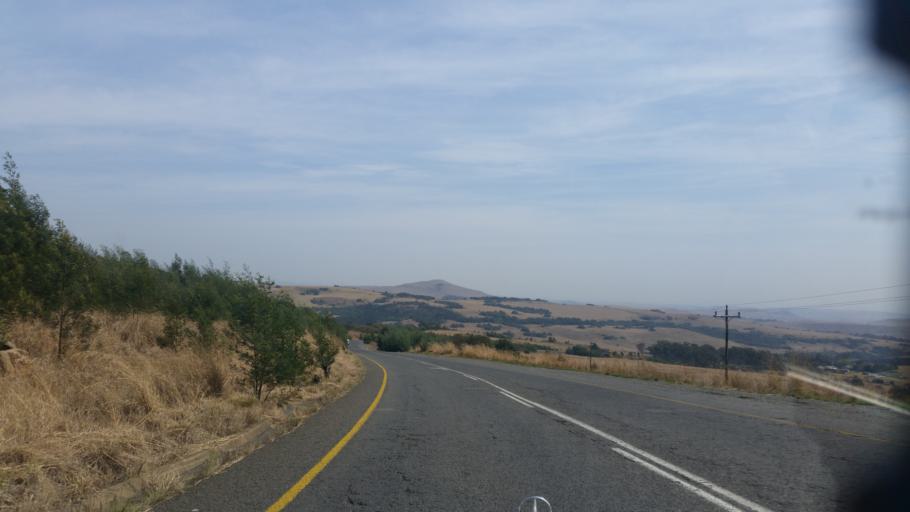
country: ZA
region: KwaZulu-Natal
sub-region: uMgungundlovu District Municipality
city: Mooirivier
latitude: -29.0958
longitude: 29.9722
